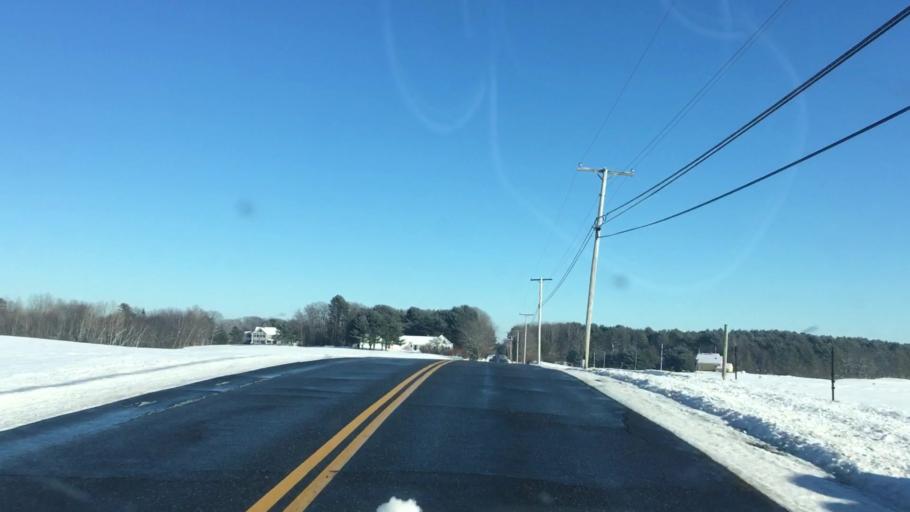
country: US
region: Maine
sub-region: Androscoggin County
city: Lisbon Falls
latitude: 43.9490
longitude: -70.1078
